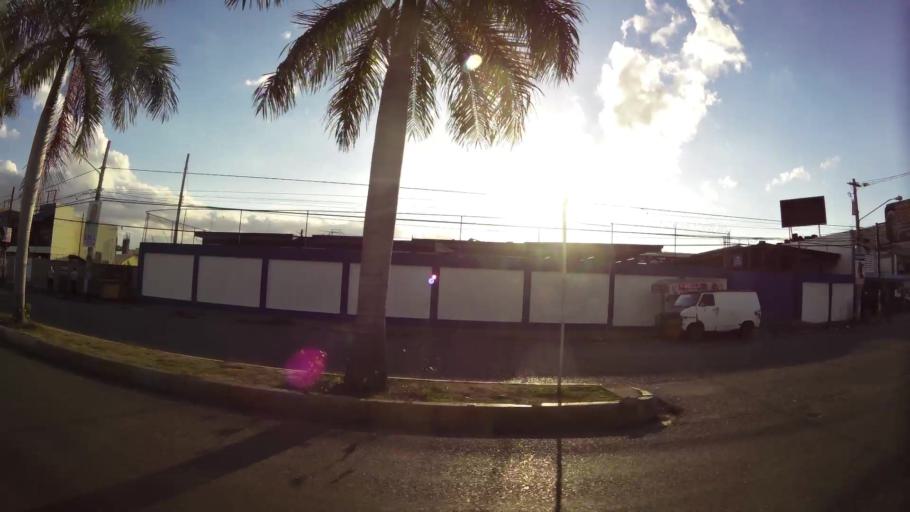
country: DO
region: Santiago
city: Santiago de los Caballeros
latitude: 19.4800
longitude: -70.7178
